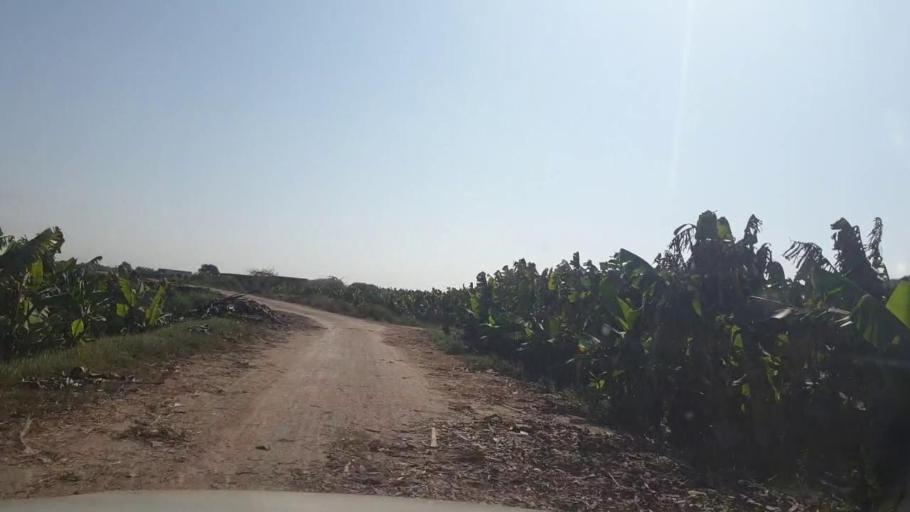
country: PK
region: Sindh
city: Chuhar Jamali
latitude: 24.4503
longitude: 67.8646
